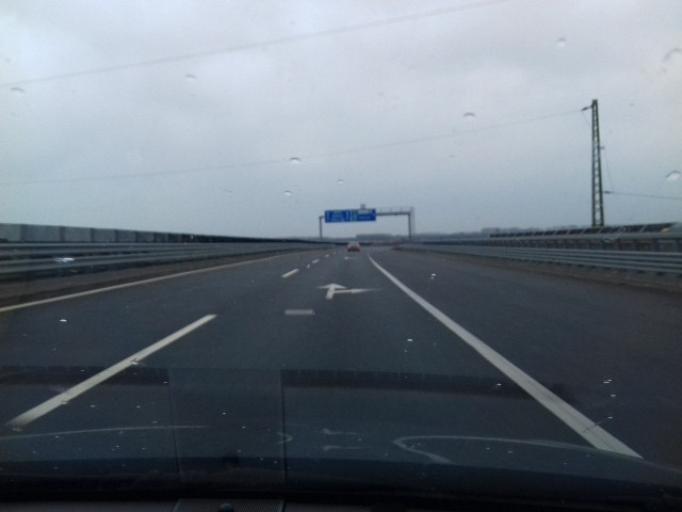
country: HU
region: Szabolcs-Szatmar-Bereg
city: Nyiregyhaza
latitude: 47.8832
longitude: 21.7143
